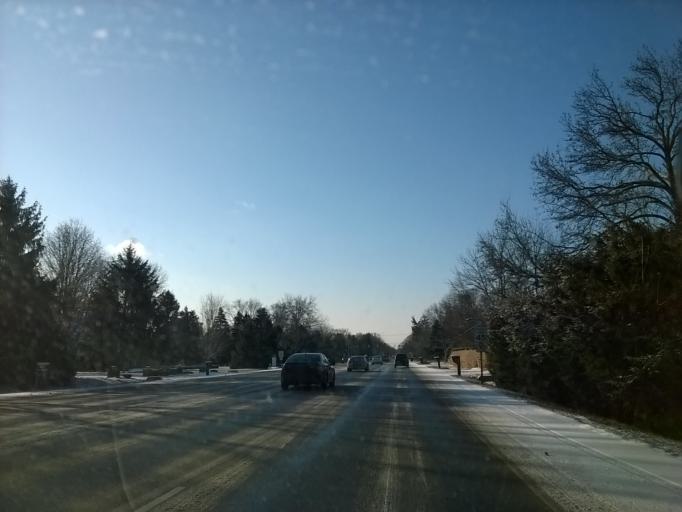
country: US
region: Indiana
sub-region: Marion County
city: Meridian Hills
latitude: 39.8927
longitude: -86.1579
